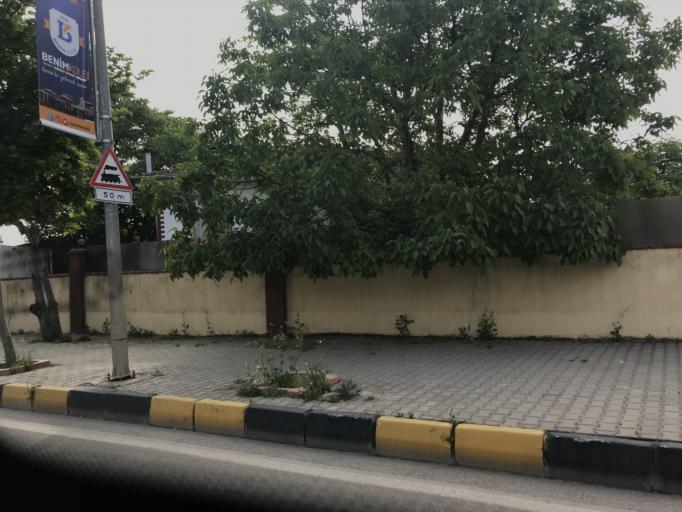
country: TR
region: Gaziantep
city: Sahinbey
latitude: 37.0678
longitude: 37.3377
